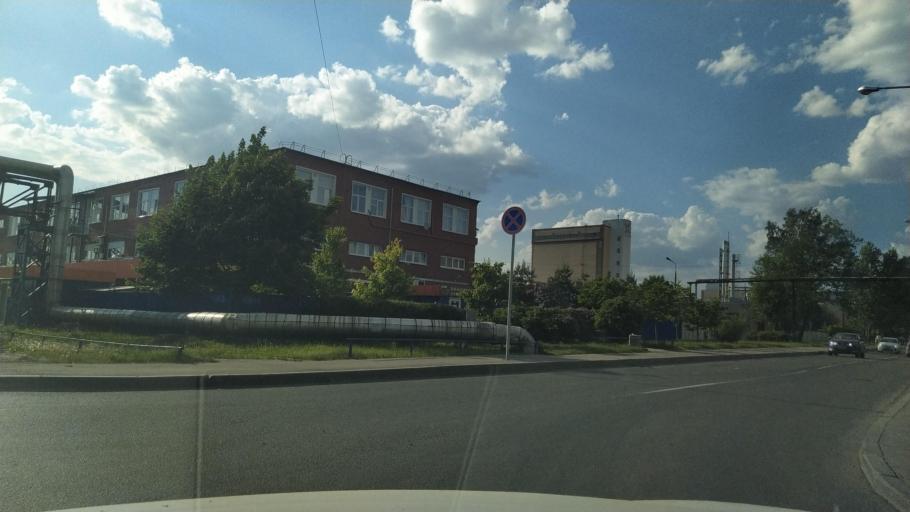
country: RU
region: St.-Petersburg
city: Dachnoye
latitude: 59.8277
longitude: 30.3082
